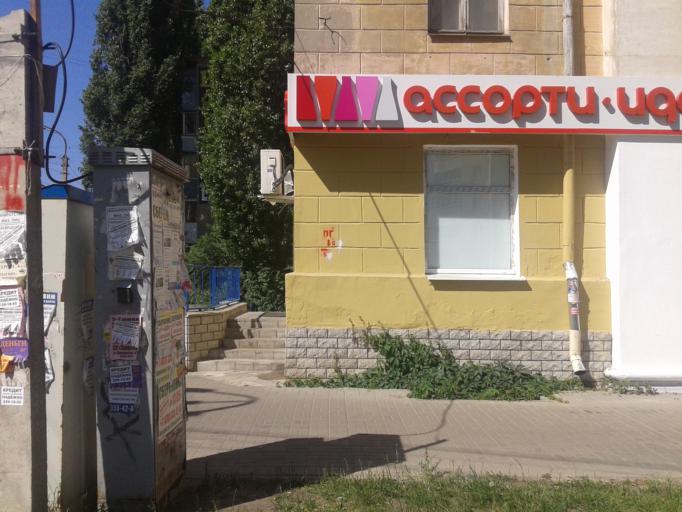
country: RU
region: Voronezj
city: Voronezh
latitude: 51.6537
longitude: 39.1769
